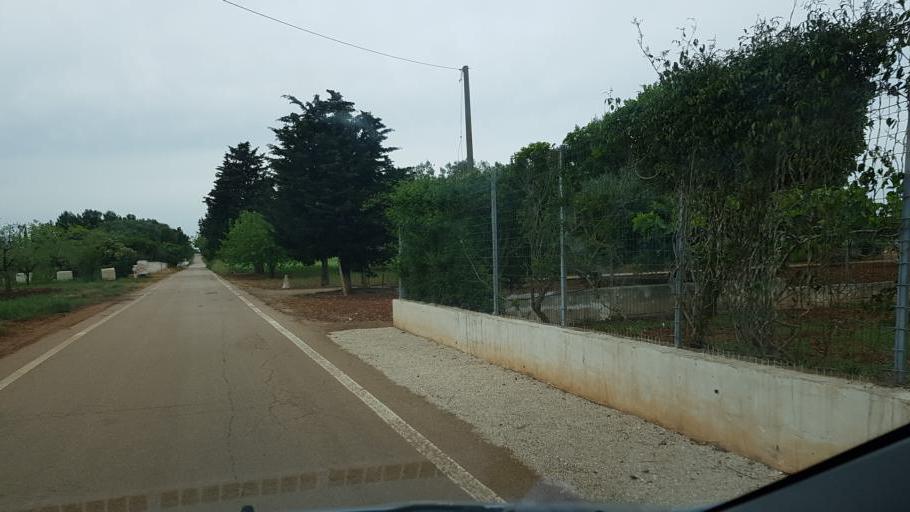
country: IT
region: Apulia
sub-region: Provincia di Brindisi
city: San Vito dei Normanni
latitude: 40.6659
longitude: 17.7736
